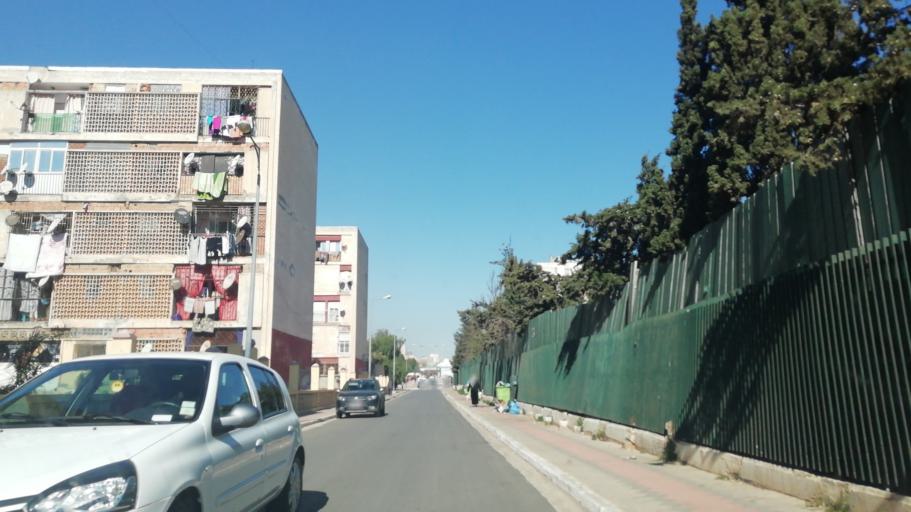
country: DZ
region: Oran
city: Oran
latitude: 35.6796
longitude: -0.6390
